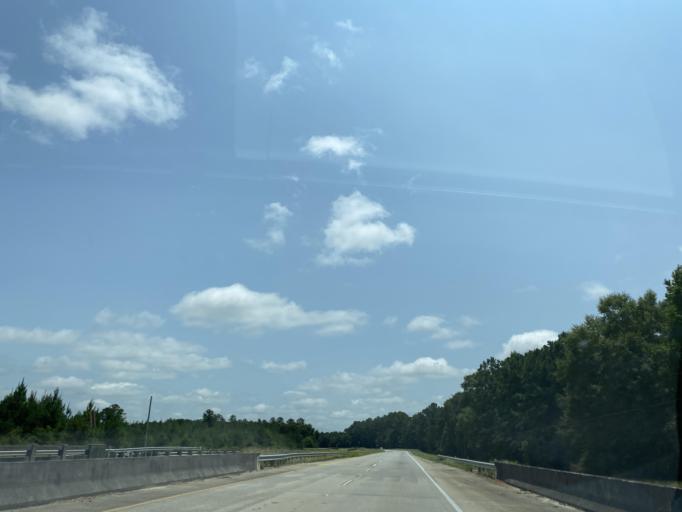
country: US
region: Georgia
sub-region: Telfair County
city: Lumber City
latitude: 31.9124
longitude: -82.6701
